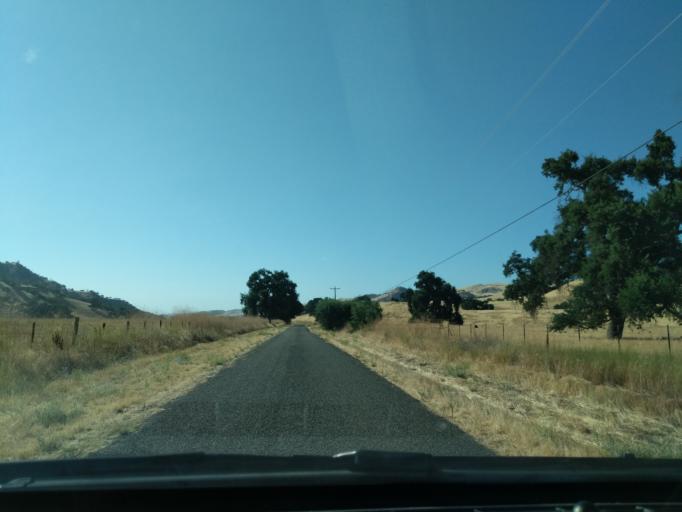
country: US
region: California
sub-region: Monterey County
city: King City
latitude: 36.1370
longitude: -120.7490
